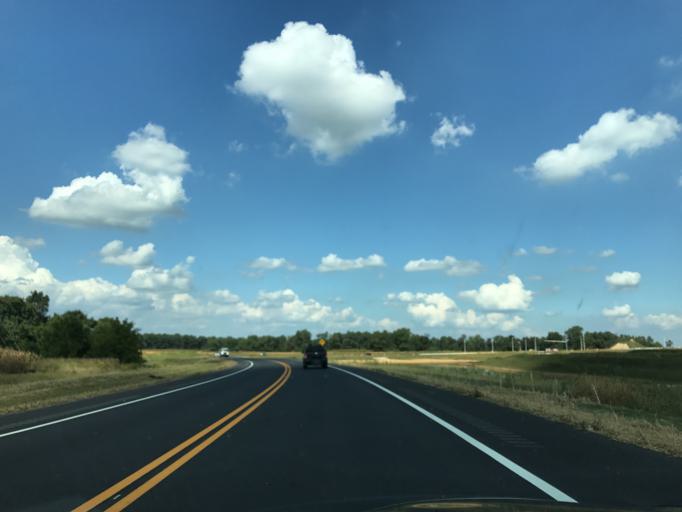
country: US
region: Delaware
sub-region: New Castle County
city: Middletown
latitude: 39.4424
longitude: -75.7555
